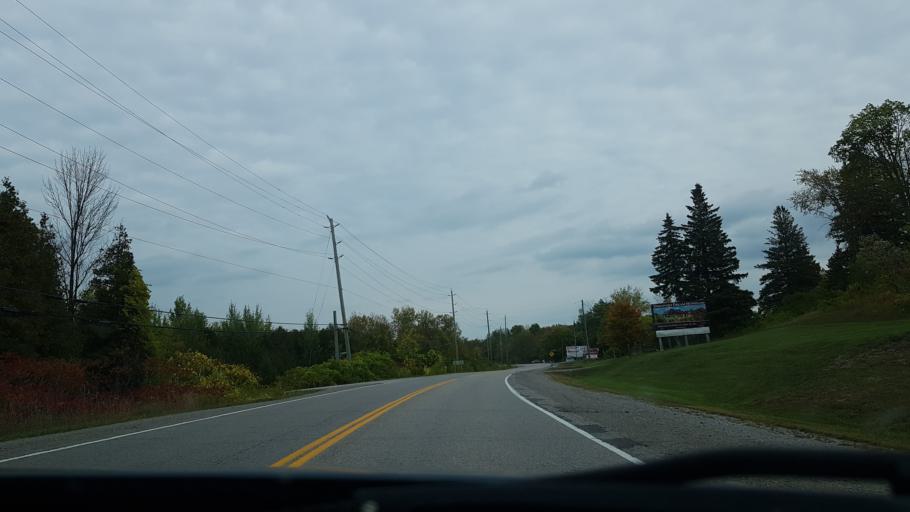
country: CA
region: Ontario
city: Omemee
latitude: 44.5248
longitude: -78.7662
